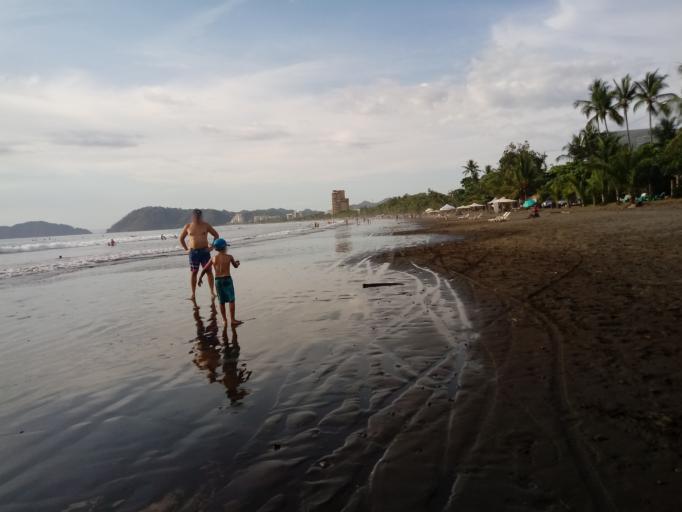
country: CR
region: Puntarenas
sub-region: Canton de Garabito
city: Jaco
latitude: 9.6002
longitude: -84.6205
